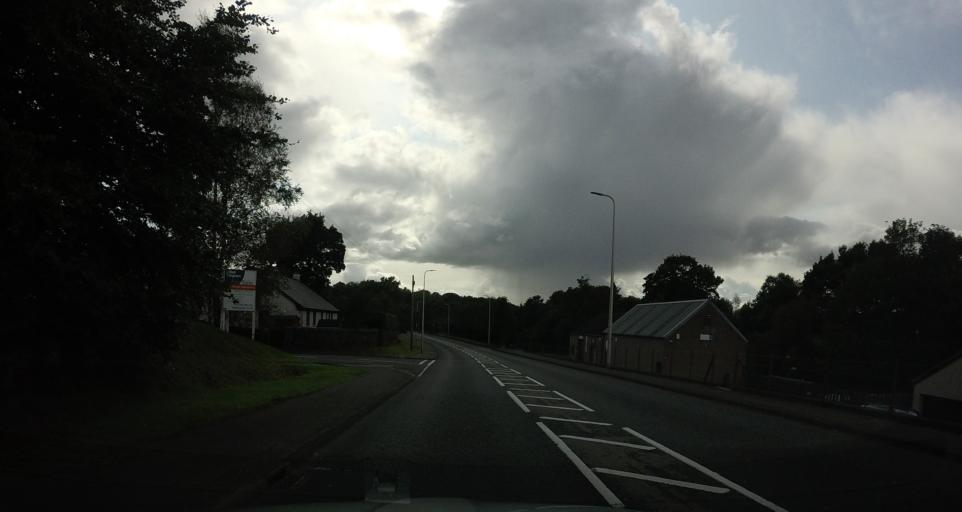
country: GB
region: Scotland
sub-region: Fife
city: Saline
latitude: 56.1835
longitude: -3.5617
